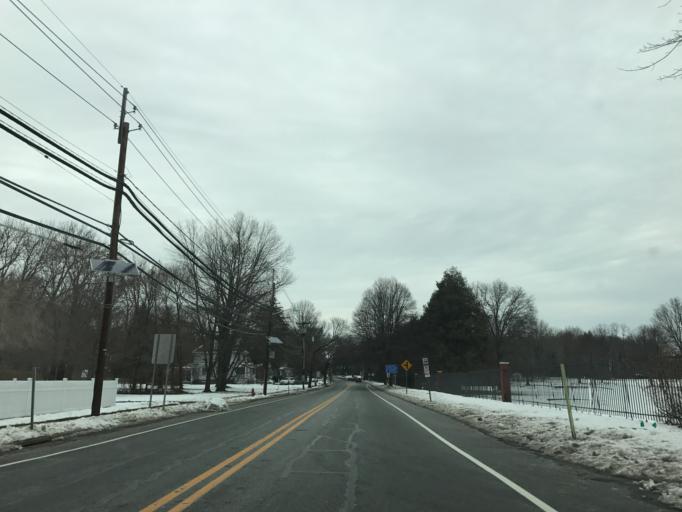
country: US
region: New Jersey
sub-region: Mercer County
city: Lawrenceville
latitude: 40.2998
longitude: -74.7277
